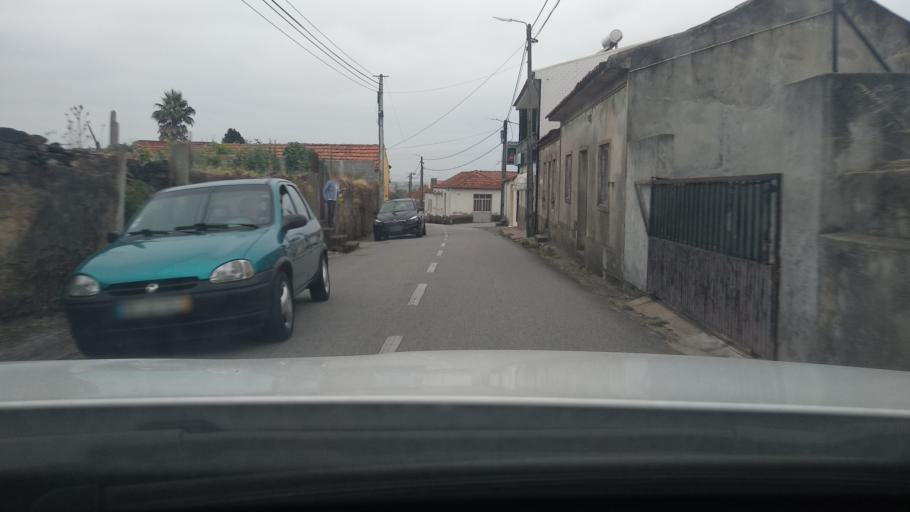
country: PT
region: Aveiro
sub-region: Espinho
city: Souto
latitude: 40.9795
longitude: -8.6283
